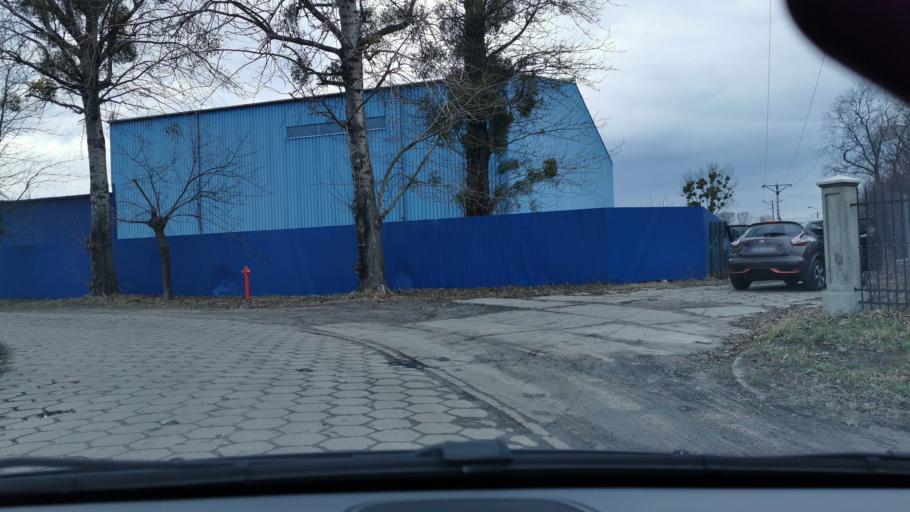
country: PL
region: Masovian Voivodeship
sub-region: Powiat zyrardowski
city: Guzow
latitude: 52.1126
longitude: 20.3333
